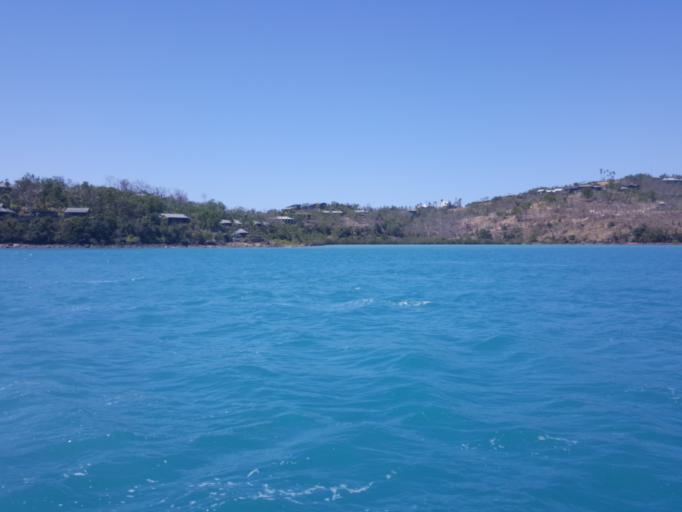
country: AU
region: Queensland
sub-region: Whitsunday
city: Proserpine
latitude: -20.3341
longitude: 148.9436
